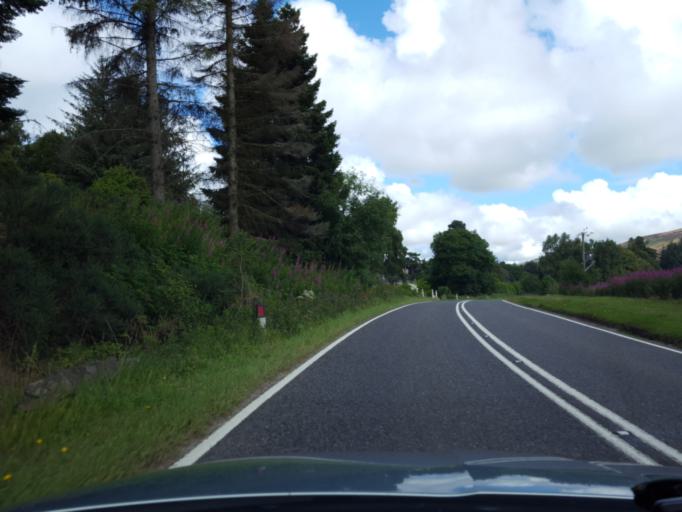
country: GB
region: Scotland
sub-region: Moray
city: Rothes
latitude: 57.5534
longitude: -3.2448
